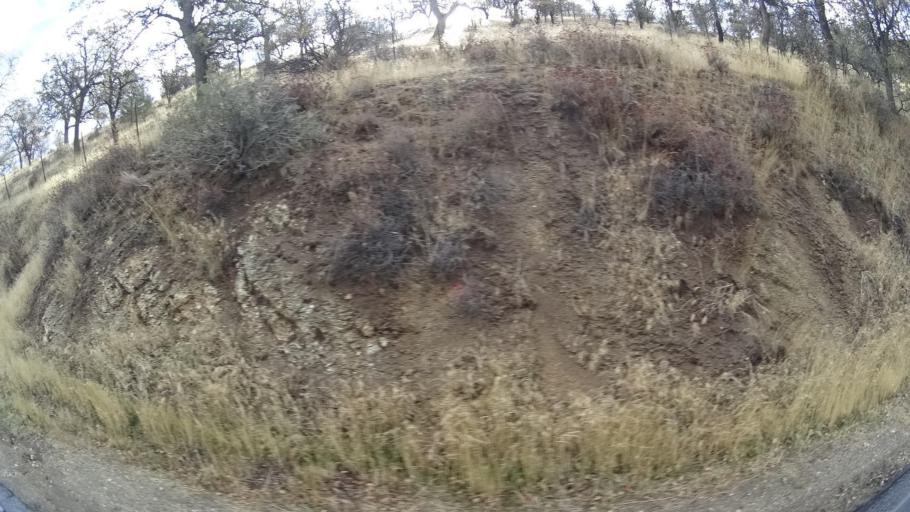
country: US
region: California
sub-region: Kern County
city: Golden Hills
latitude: 35.1942
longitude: -118.5297
